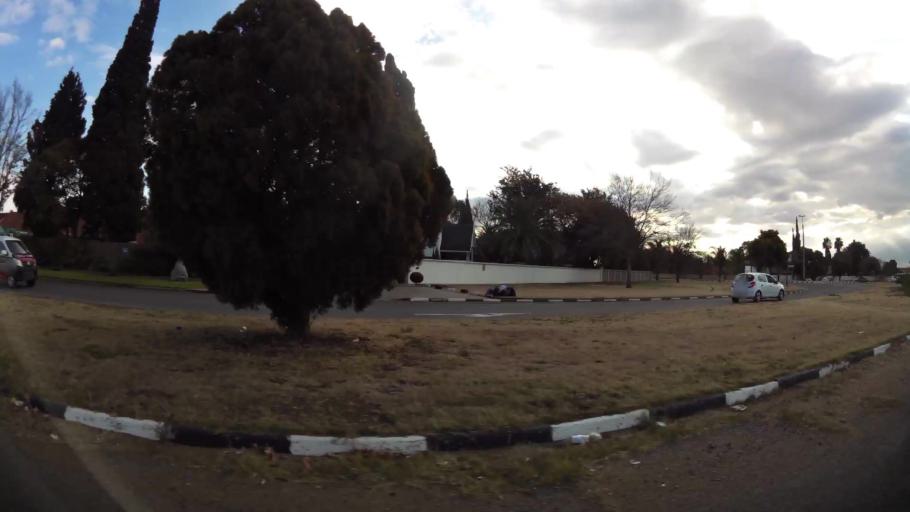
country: ZA
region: Orange Free State
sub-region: Lejweleputswa District Municipality
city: Welkom
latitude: -27.9920
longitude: 26.7319
